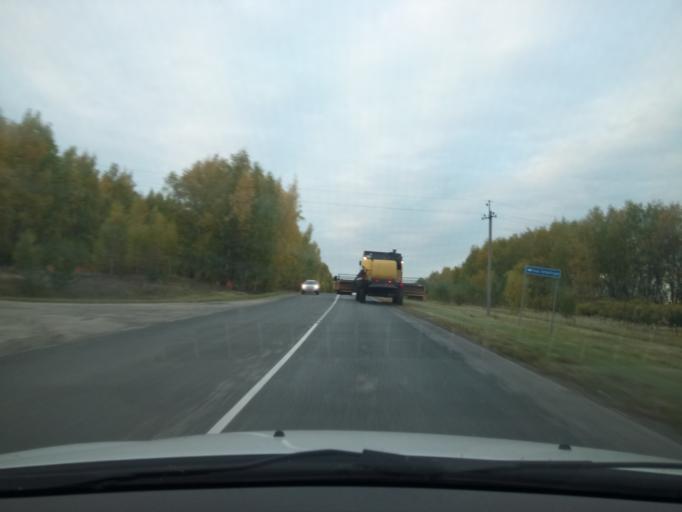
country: RU
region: Nizjnij Novgorod
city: Bol'shoye Murashkino
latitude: 55.7303
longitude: 44.7753
